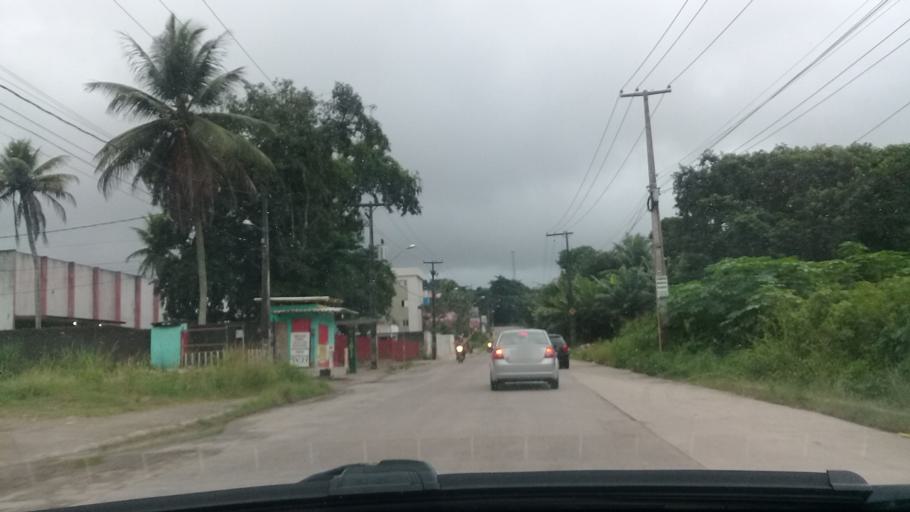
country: BR
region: Pernambuco
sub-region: Moreno
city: Moreno
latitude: -8.1153
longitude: -35.0850
